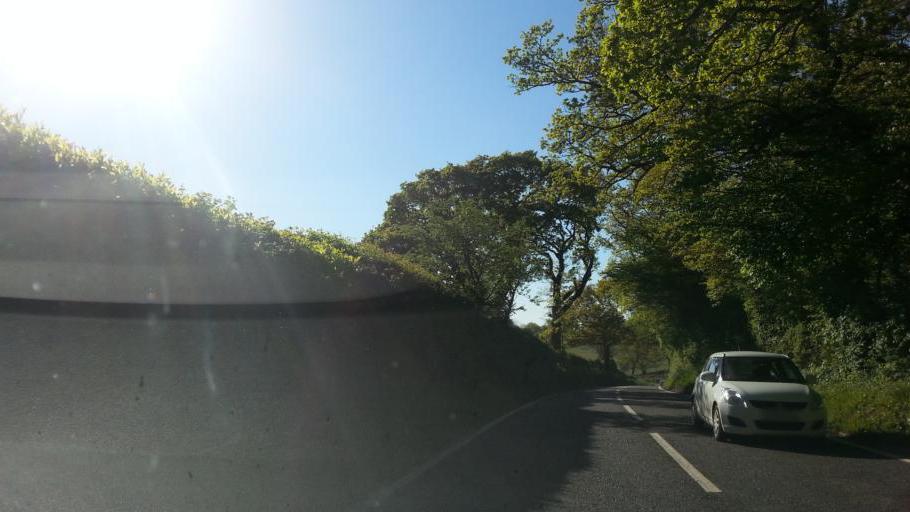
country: GB
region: England
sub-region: Somerset
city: Castle Cary
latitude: 51.0640
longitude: -2.4730
